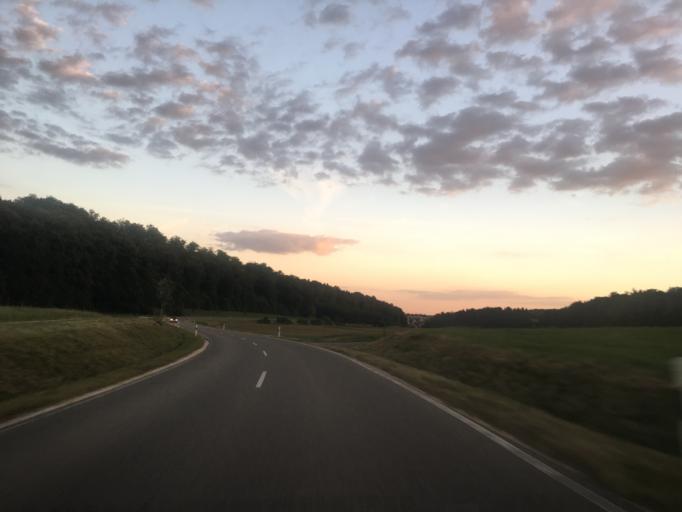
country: DE
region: Baden-Wuerttemberg
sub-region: Tuebingen Region
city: Gomadingen
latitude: 48.3392
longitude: 9.4330
